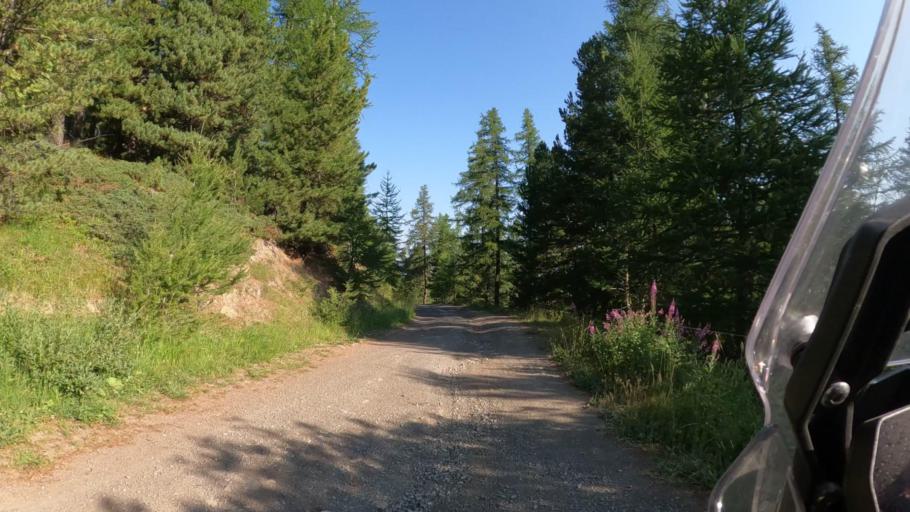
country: FR
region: Provence-Alpes-Cote d'Azur
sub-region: Departement des Hautes-Alpes
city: Guillestre
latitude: 44.6164
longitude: 6.6470
